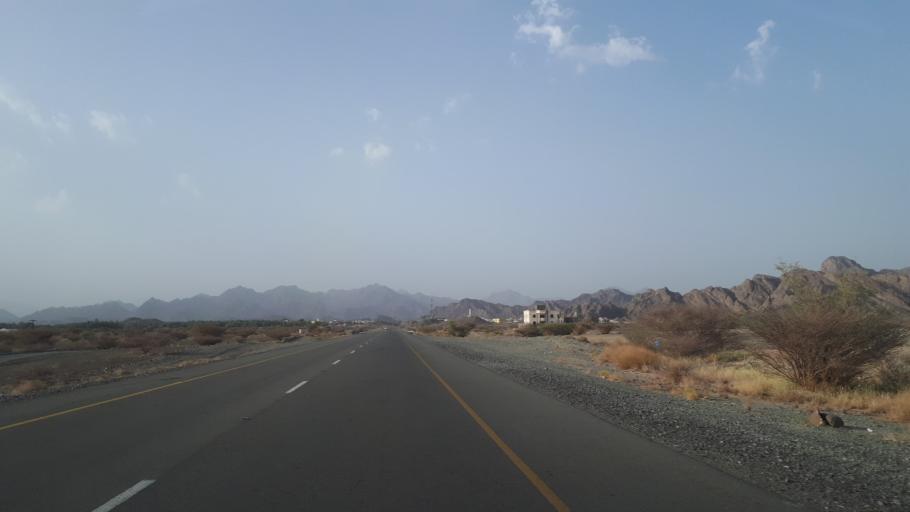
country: OM
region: Az Zahirah
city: Yanqul
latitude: 23.4517
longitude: 56.7906
